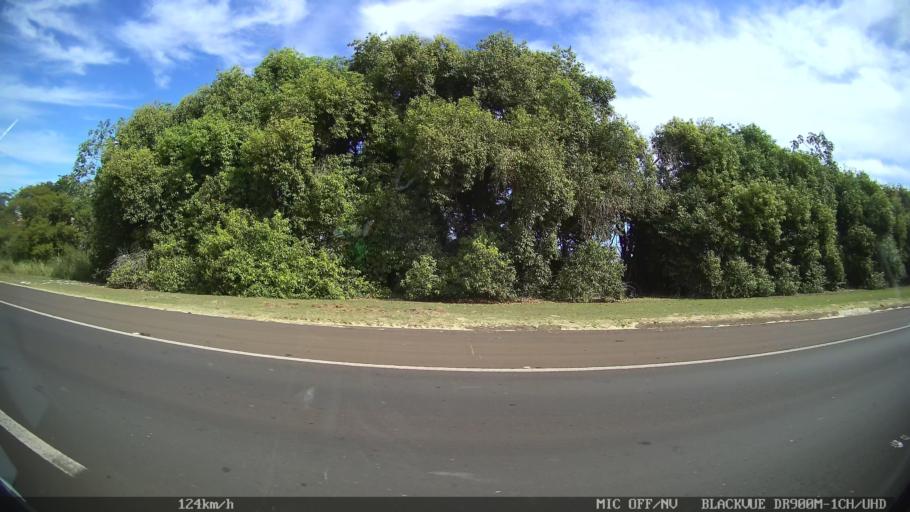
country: BR
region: Sao Paulo
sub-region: Matao
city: Matao
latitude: -21.6130
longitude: -48.4212
